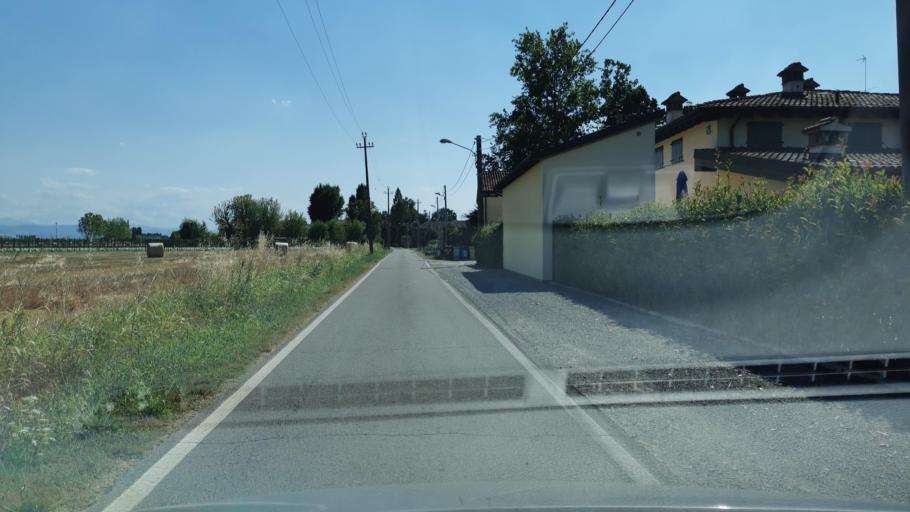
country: IT
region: Emilia-Romagna
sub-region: Provincia di Modena
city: Villanova
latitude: 44.6921
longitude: 10.9023
